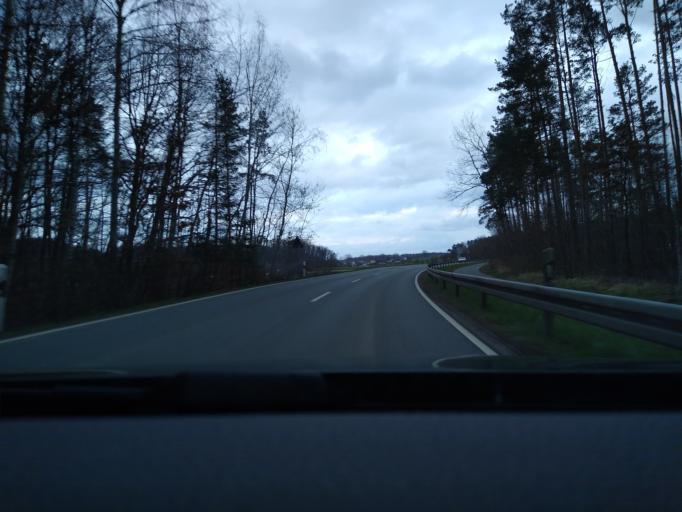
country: DE
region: Bavaria
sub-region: Regierungsbezirk Mittelfranken
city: Zirndorf
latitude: 49.4576
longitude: 10.9163
